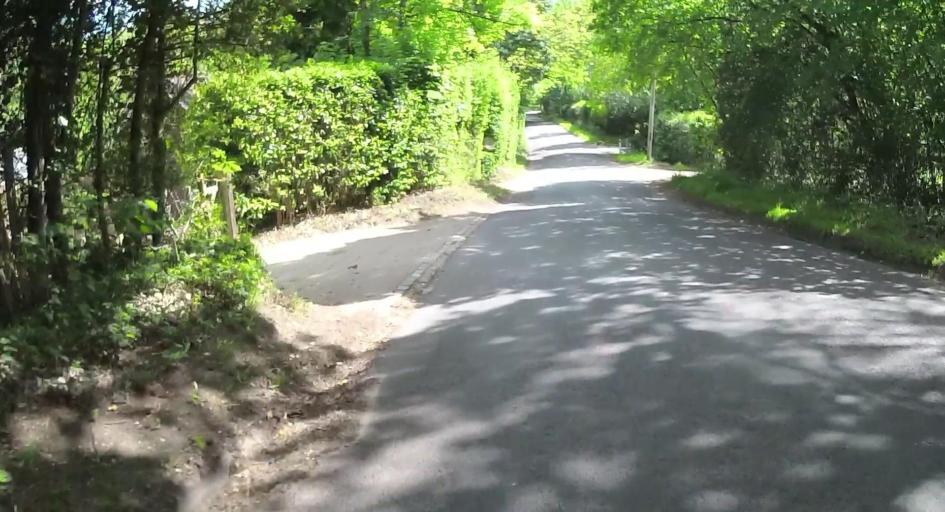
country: GB
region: England
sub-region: Surrey
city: Farnham
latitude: 51.1859
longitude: -0.8016
